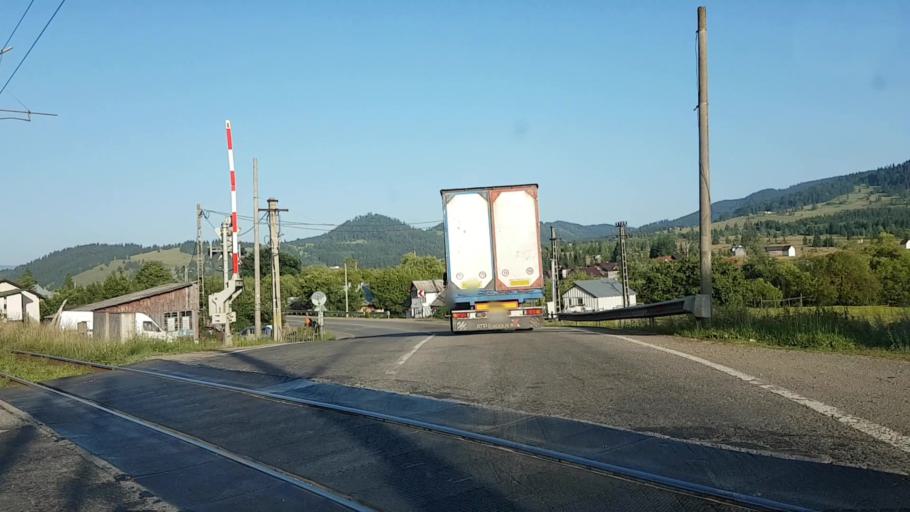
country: RO
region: Suceava
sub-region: Comuna Dorna Candrenilor
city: Dorna Candrenilor
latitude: 47.3573
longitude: 25.2355
